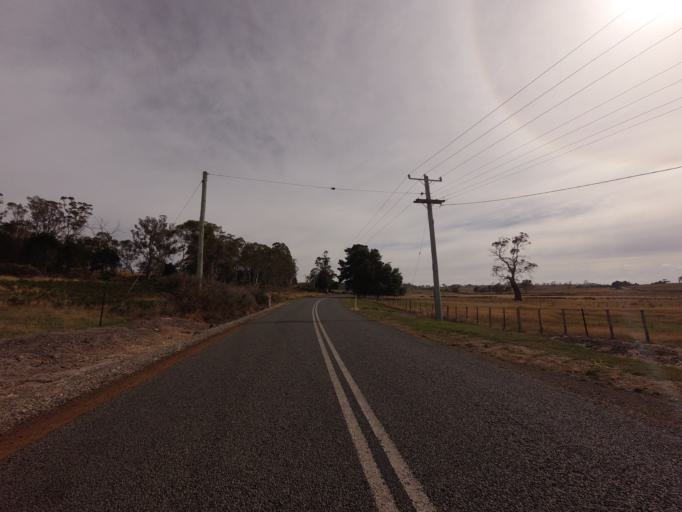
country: AU
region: Tasmania
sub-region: Brighton
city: Bridgewater
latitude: -42.3468
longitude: 147.4043
